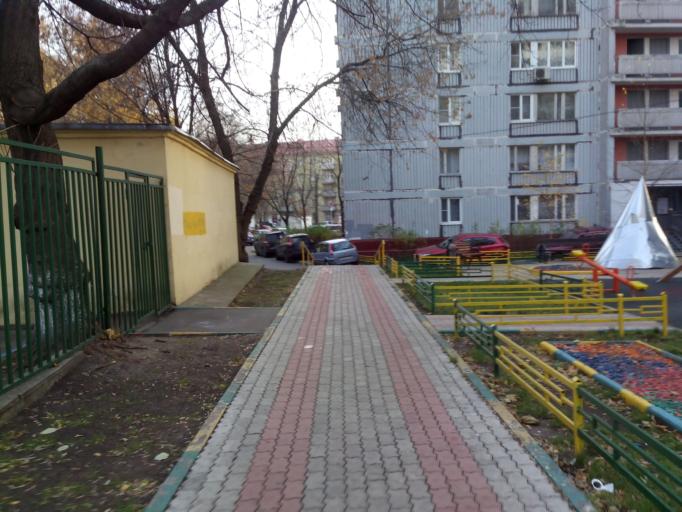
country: RU
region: Moscow
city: Lefortovo
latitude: 55.7656
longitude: 37.7160
